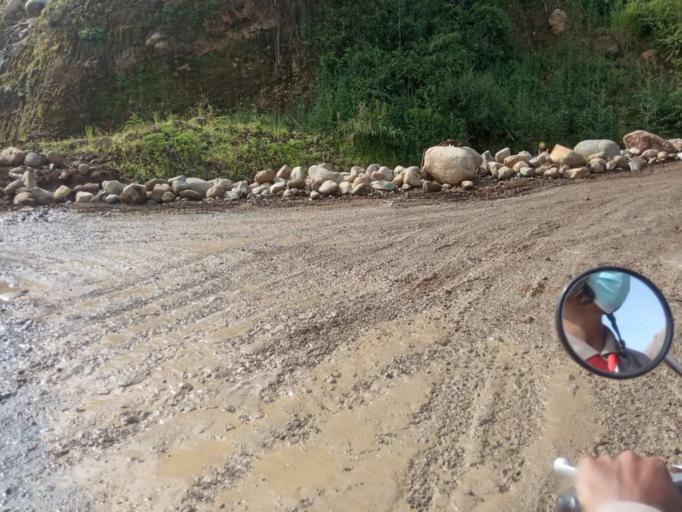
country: ID
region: West Java
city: Caringin
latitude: -6.6593
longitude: 106.8839
